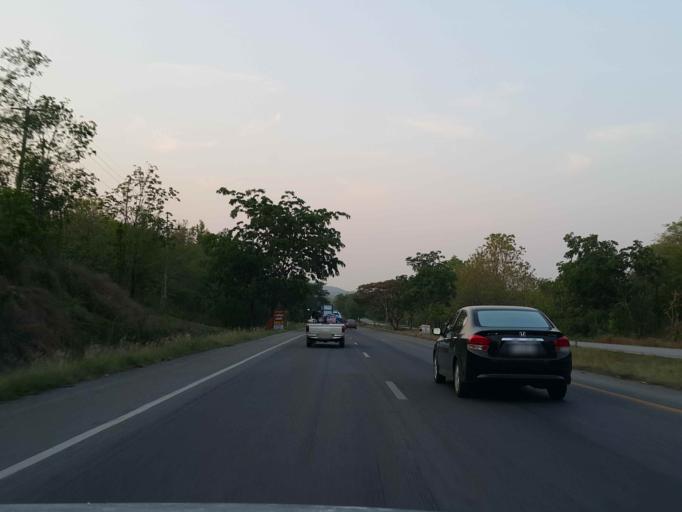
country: TH
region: Lampang
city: Ko Kha
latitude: 18.0575
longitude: 99.3895
